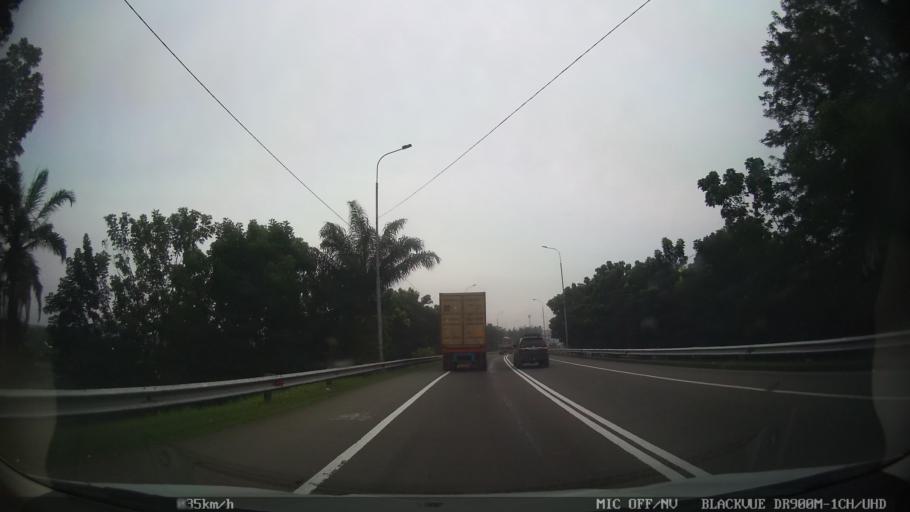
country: ID
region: North Sumatra
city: Deli Tua
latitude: 3.5431
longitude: 98.7263
